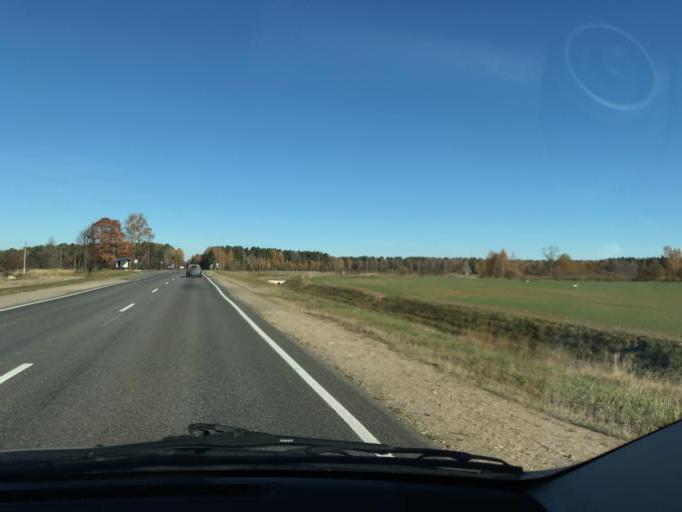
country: BY
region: Vitebsk
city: Lyepyel'
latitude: 55.0550
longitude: 28.7517
